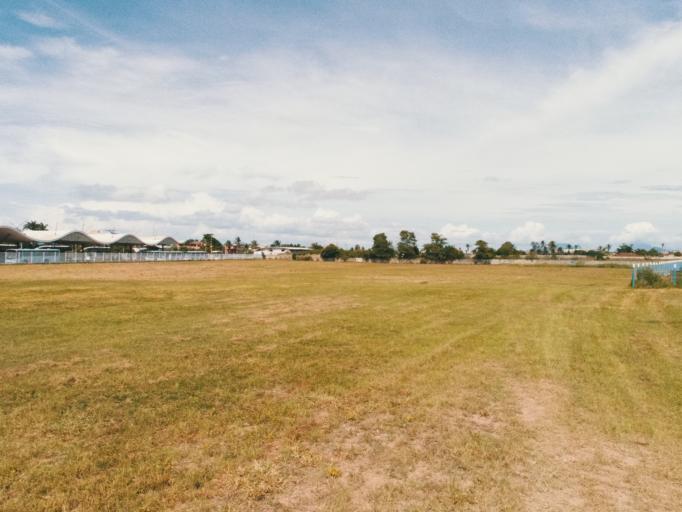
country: BR
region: Rio de Janeiro
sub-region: Macae
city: Macae
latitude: -22.3298
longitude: -41.7531
